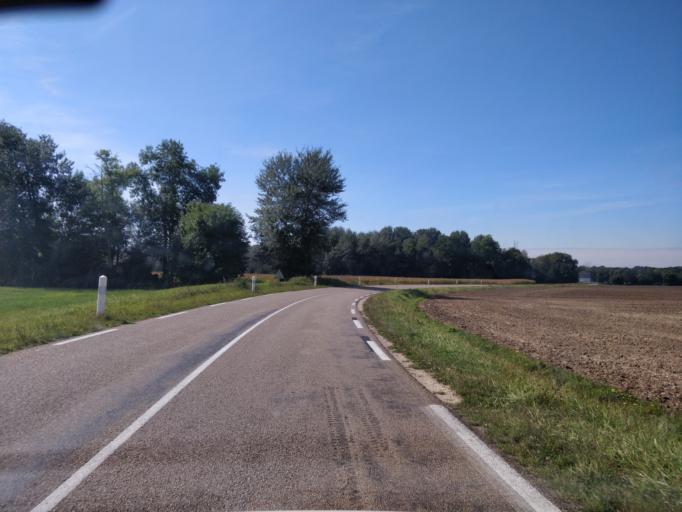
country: FR
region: Bourgogne
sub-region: Departement de l'Yonne
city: Saint-Florentin
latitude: 48.0154
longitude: 3.6888
